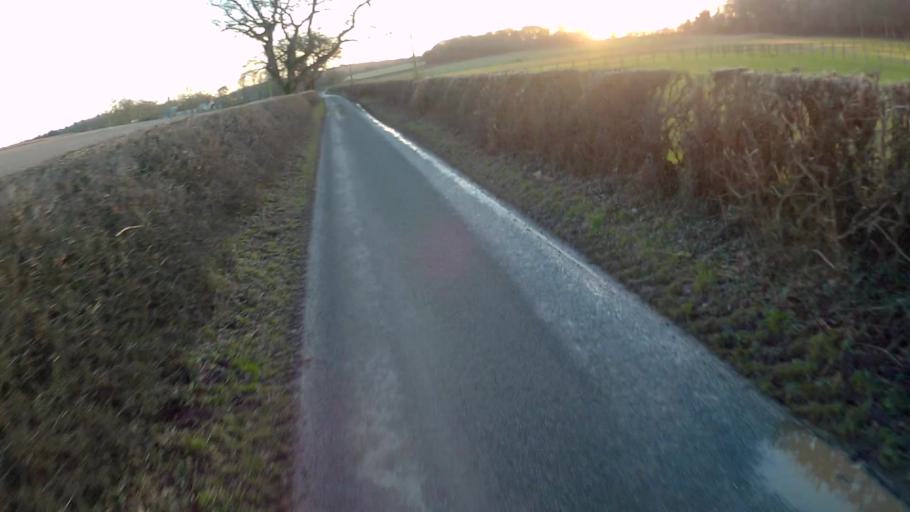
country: GB
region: England
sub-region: Hampshire
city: Overton
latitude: 51.2100
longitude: -1.2321
